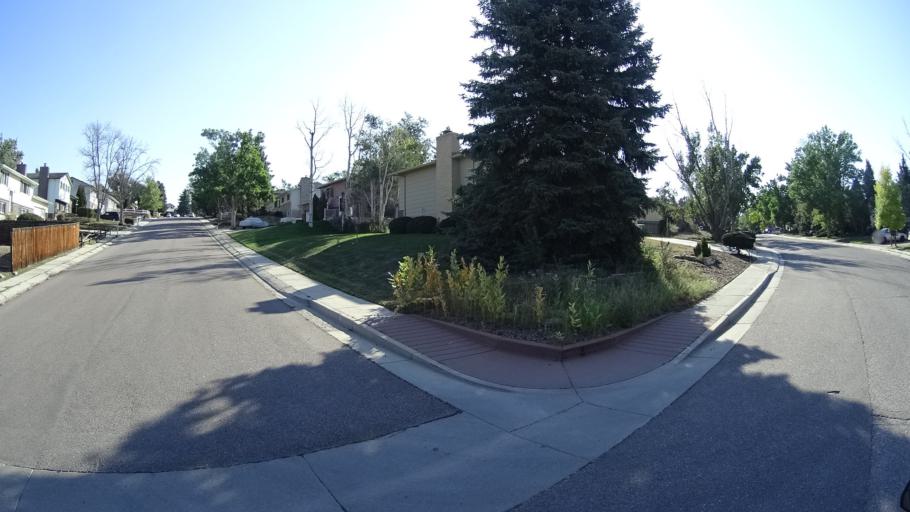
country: US
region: Colorado
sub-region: El Paso County
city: Cimarron Hills
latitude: 38.8801
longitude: -104.7366
